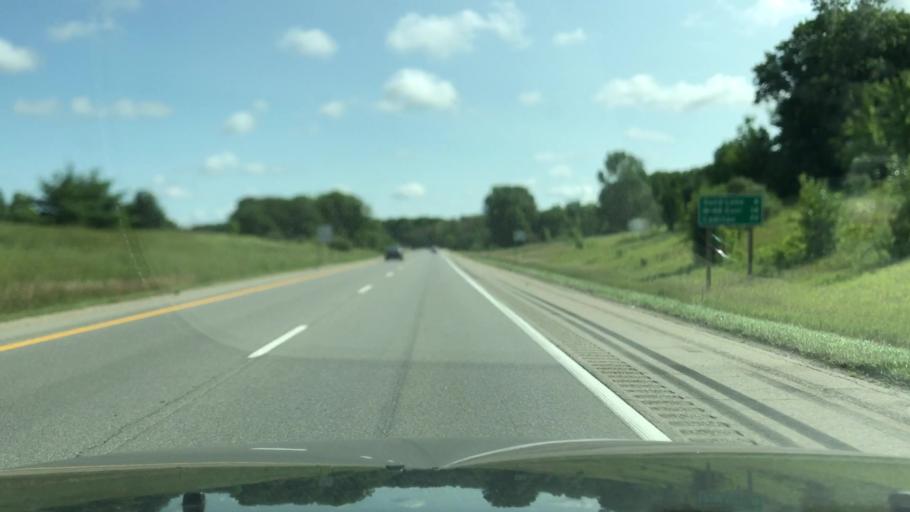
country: US
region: Michigan
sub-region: Kent County
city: Cedar Springs
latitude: 43.2324
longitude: -85.5669
